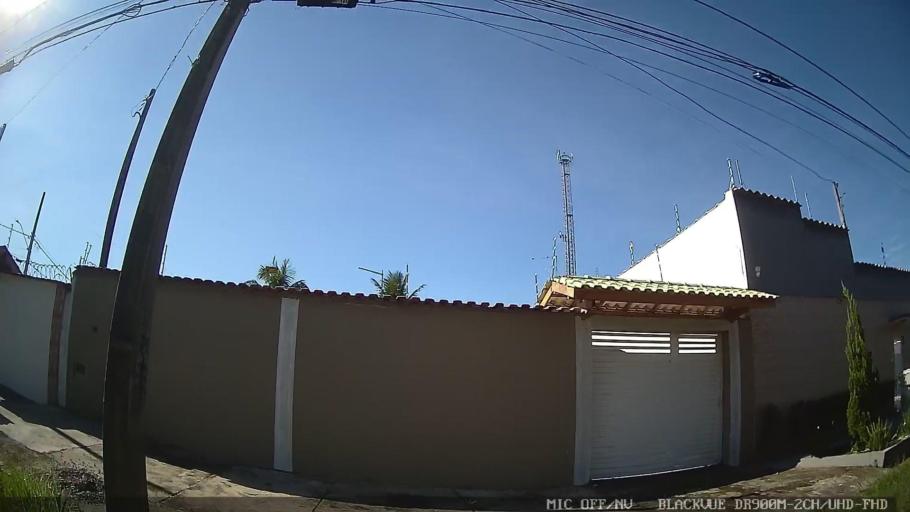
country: BR
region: Sao Paulo
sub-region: Itanhaem
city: Itanhaem
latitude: -24.2235
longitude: -46.8779
